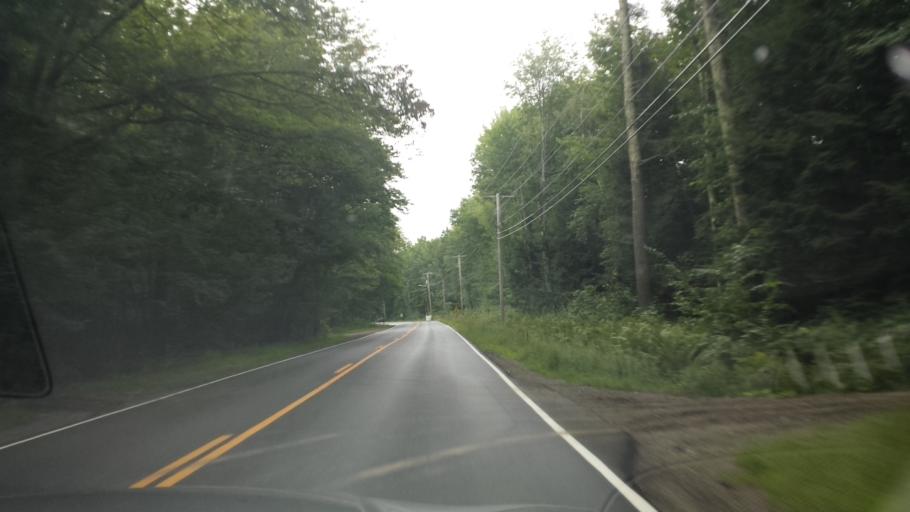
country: US
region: Maine
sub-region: York County
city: South Sanford
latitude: 43.4006
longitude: -70.6793
